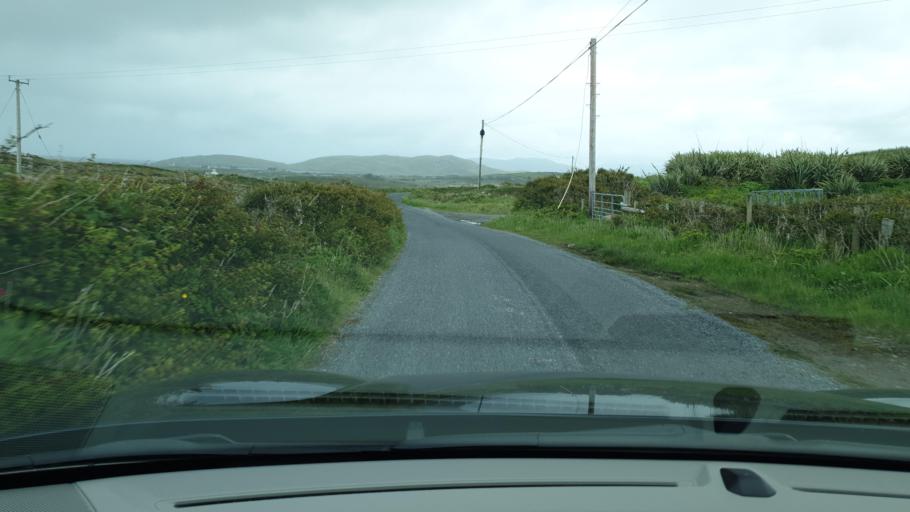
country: IE
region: Connaught
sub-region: County Galway
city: Clifden
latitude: 53.5510
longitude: -10.1671
